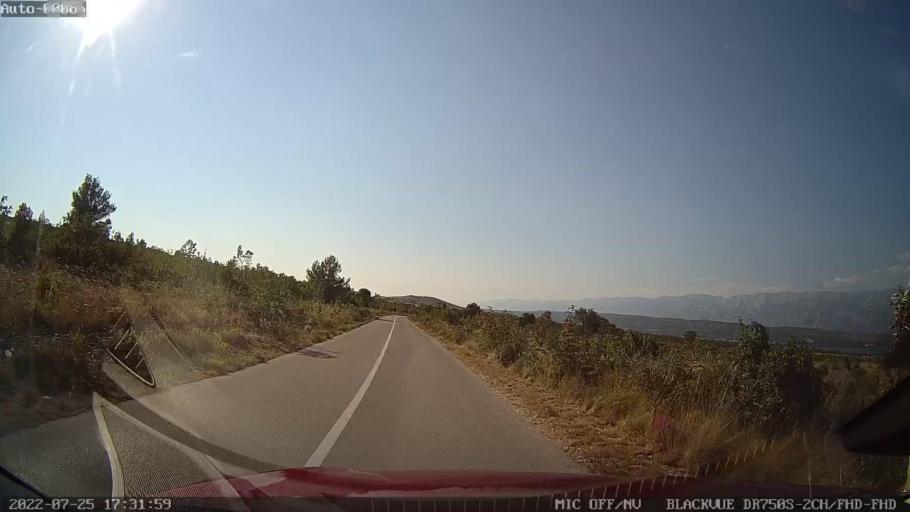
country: HR
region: Zadarska
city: Posedarje
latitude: 44.1736
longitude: 15.4965
